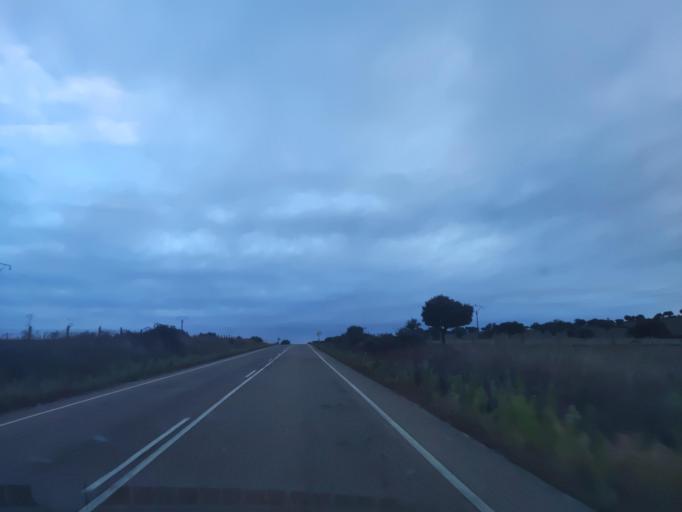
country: ES
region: Castille and Leon
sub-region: Provincia de Salamanca
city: San Felices de los Gallegos
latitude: 40.8790
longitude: -6.7120
